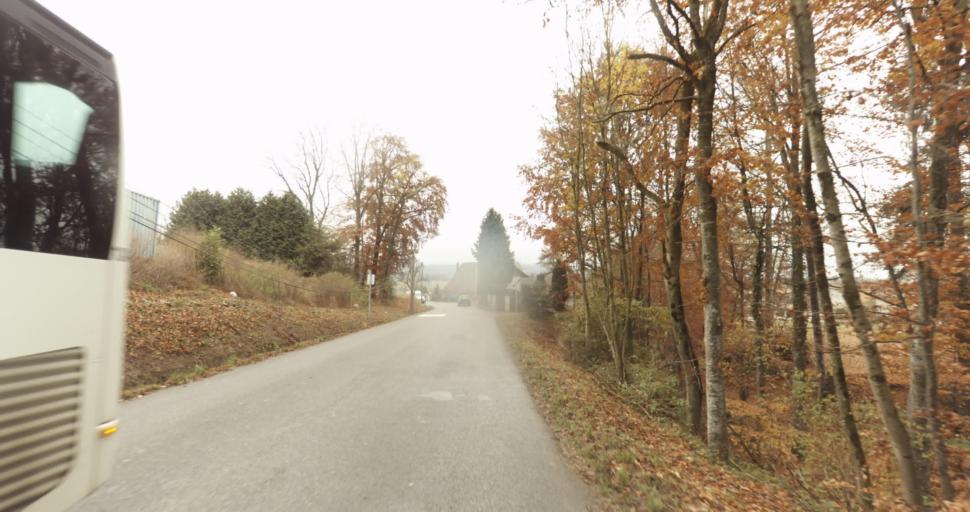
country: FR
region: Rhone-Alpes
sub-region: Departement de la Haute-Savoie
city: Evires
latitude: 46.0525
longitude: 6.2107
